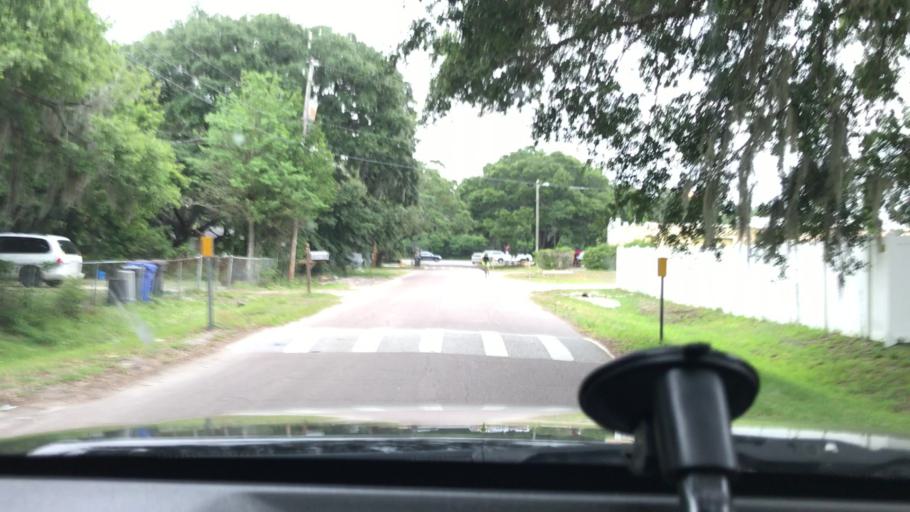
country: US
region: Florida
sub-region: Hillsborough County
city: Riverview
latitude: 27.8606
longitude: -82.3283
